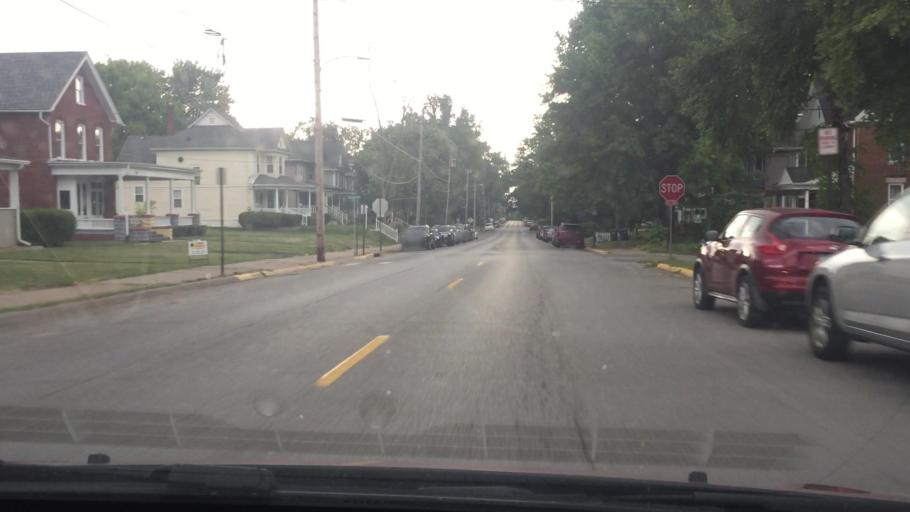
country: US
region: Iowa
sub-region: Muscatine County
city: Muscatine
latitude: 41.4358
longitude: -91.0546
